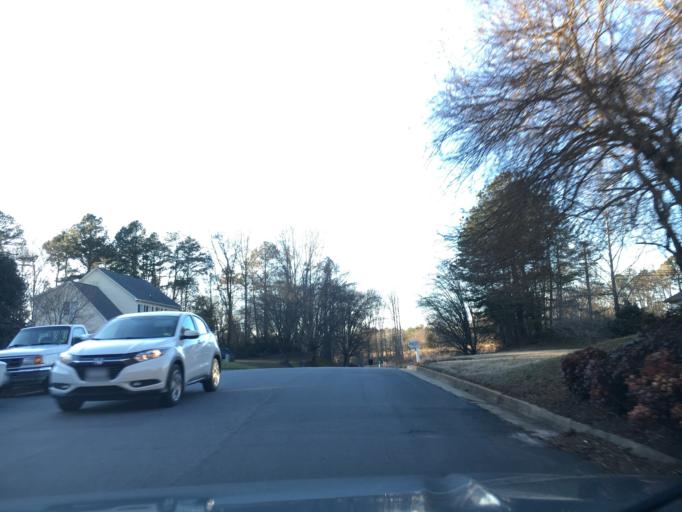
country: US
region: Virginia
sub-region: Halifax County
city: South Boston
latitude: 36.7074
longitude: -78.8850
